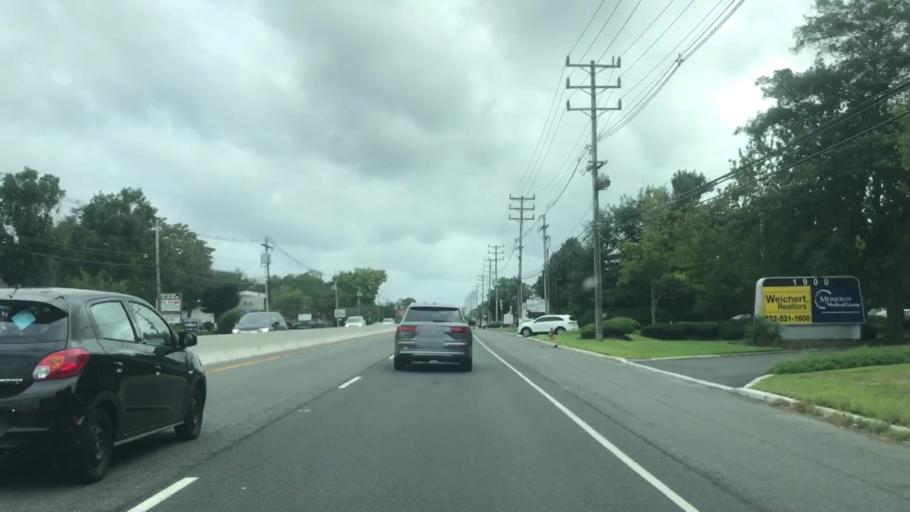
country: US
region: New Jersey
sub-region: Monmouth County
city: Oakhurst
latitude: 40.2617
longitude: -74.0415
